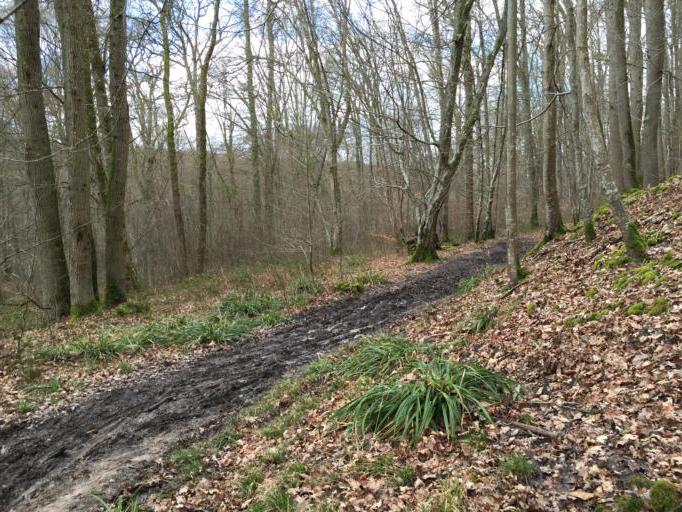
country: FR
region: Ile-de-France
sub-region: Departement des Yvelines
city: Cernay-la-Ville
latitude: 48.6791
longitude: 1.9553
